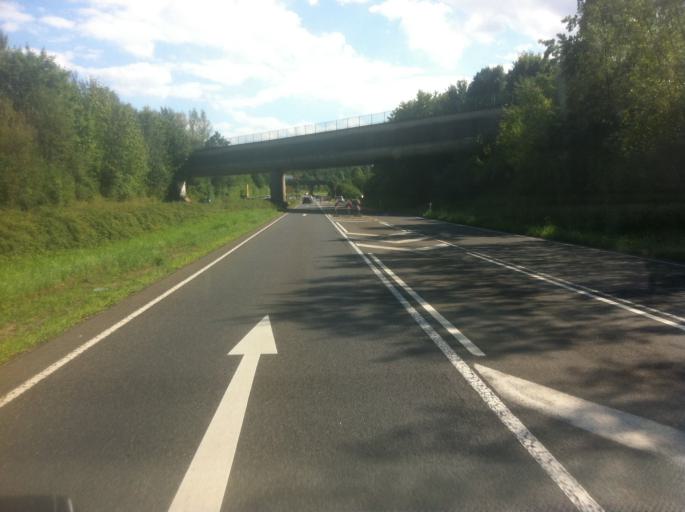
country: DE
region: North Rhine-Westphalia
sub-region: Regierungsbezirk Koln
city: Erftstadt
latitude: 50.8129
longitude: 6.8062
